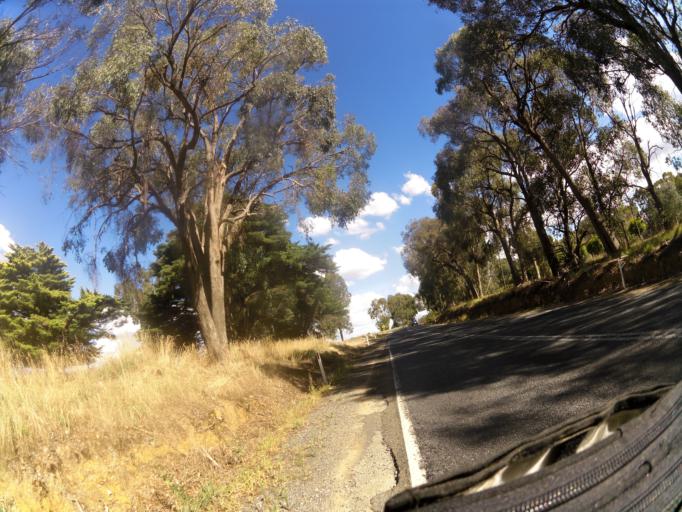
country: AU
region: Victoria
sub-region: Mansfield
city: Mansfield
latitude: -36.9242
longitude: 146.0018
